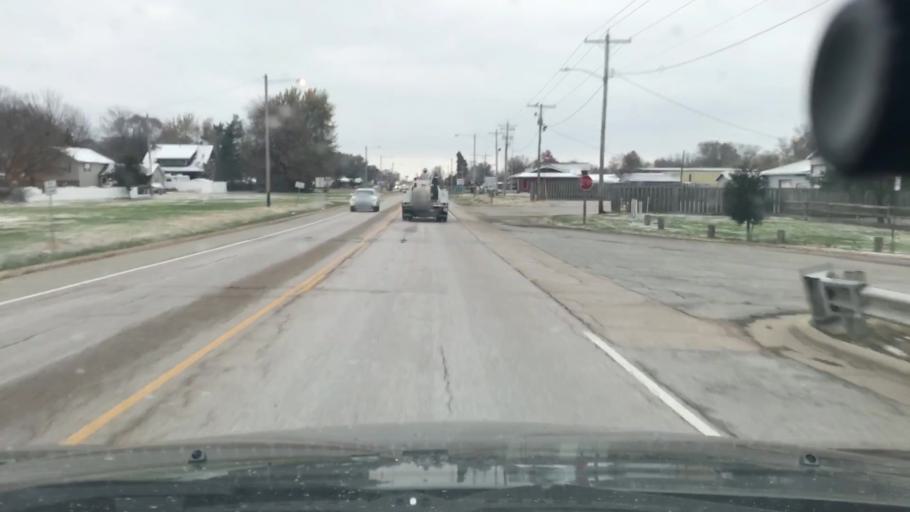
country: US
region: Illinois
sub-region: Madison County
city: Pontoon Beach
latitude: 38.7266
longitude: -90.0709
